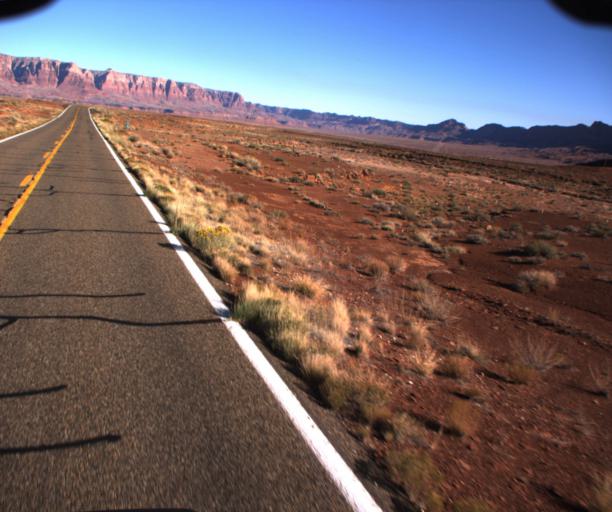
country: US
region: Arizona
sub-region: Coconino County
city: LeChee
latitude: 36.7057
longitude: -111.6565
